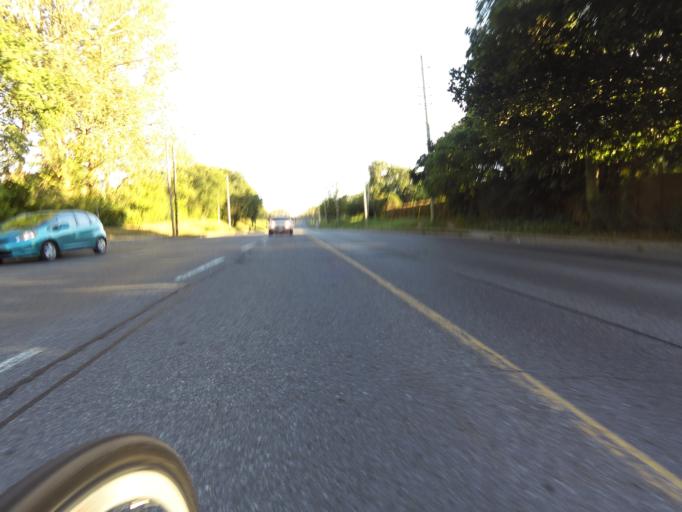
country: CA
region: Ontario
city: Bells Corners
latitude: 45.3354
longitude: -75.7849
